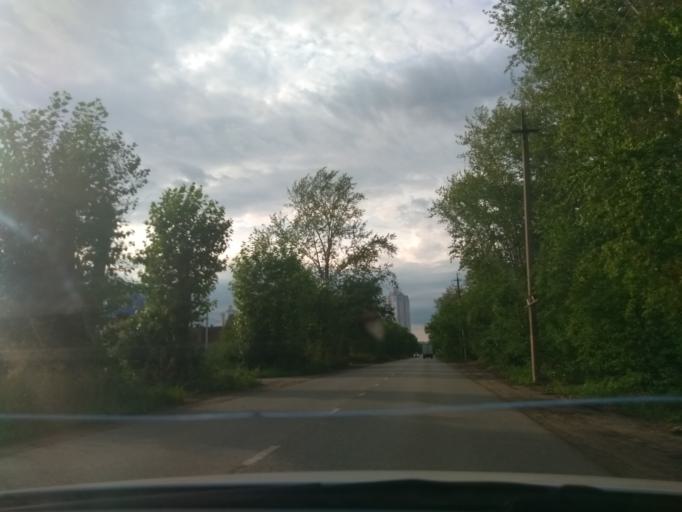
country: RU
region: Perm
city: Perm
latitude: 58.0002
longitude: 56.3328
